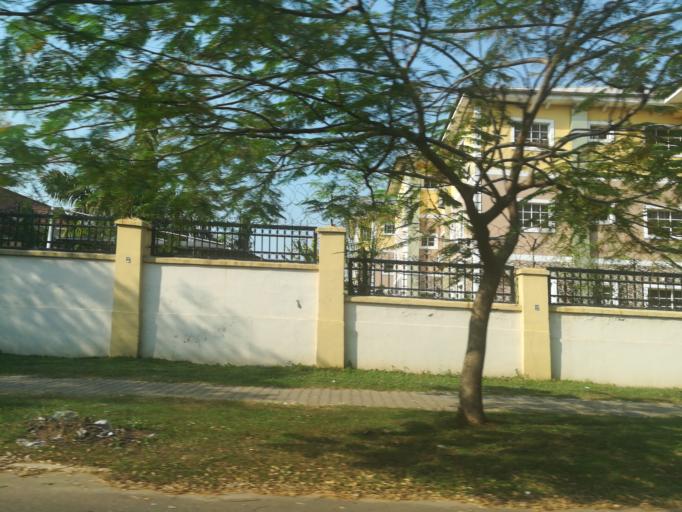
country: NG
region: Abuja Federal Capital Territory
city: Abuja
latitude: 9.0724
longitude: 7.4307
